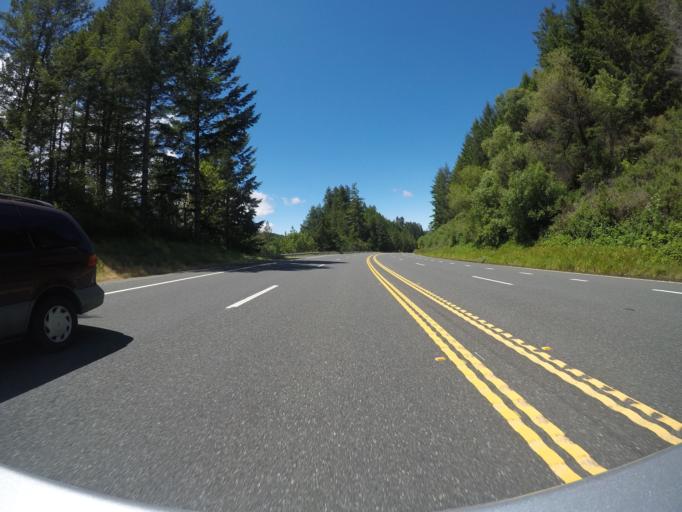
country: US
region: California
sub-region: Humboldt County
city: Redway
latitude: 39.9397
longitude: -123.7769
